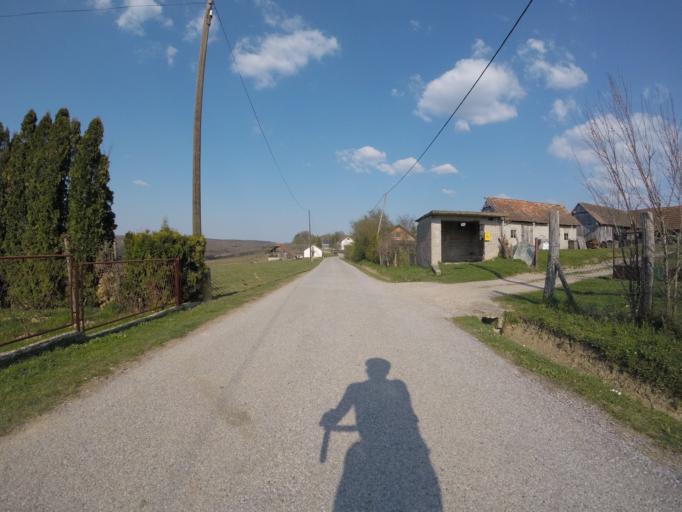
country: HR
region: Sisacko-Moslavacka
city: Glina
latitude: 45.5025
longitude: 15.9979
